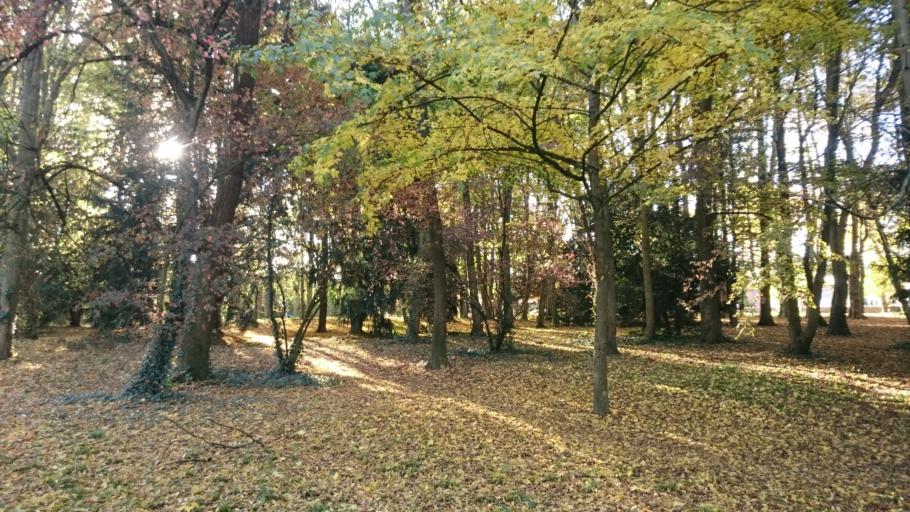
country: FR
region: Ile-de-France
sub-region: Departement de l'Essonne
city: La Ville-du-Bois
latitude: 48.6548
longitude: 2.2819
